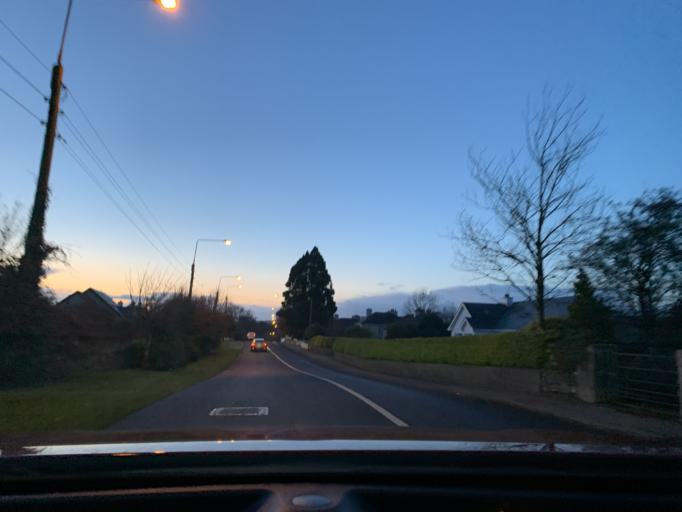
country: IE
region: Connaught
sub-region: Roscommon
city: Boyle
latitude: 53.9709
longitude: -8.2854
